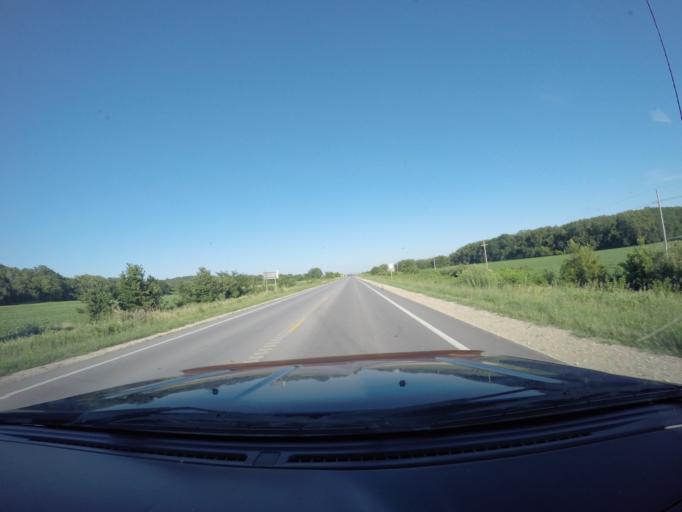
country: US
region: Kansas
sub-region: Douglas County
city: Lawrence
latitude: 39.0675
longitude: -95.3397
